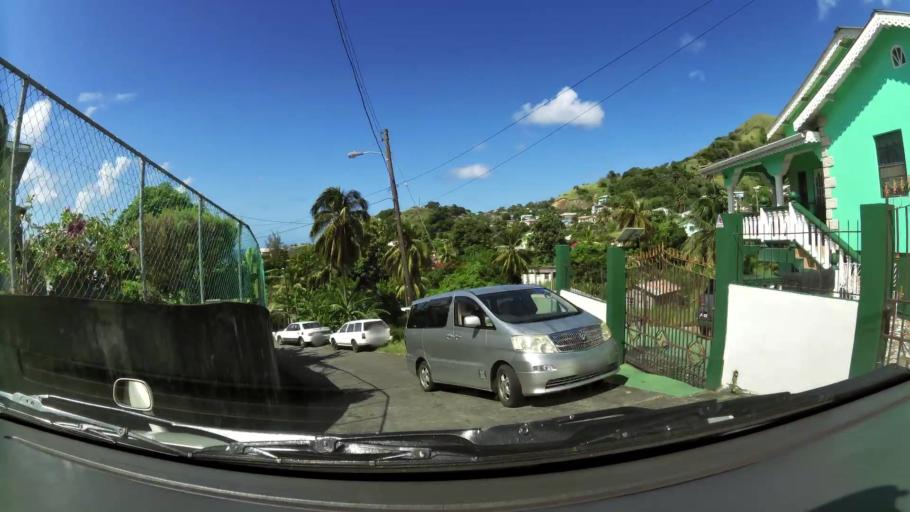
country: VC
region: Saint George
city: Kingstown Park
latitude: 13.1722
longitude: -61.2393
